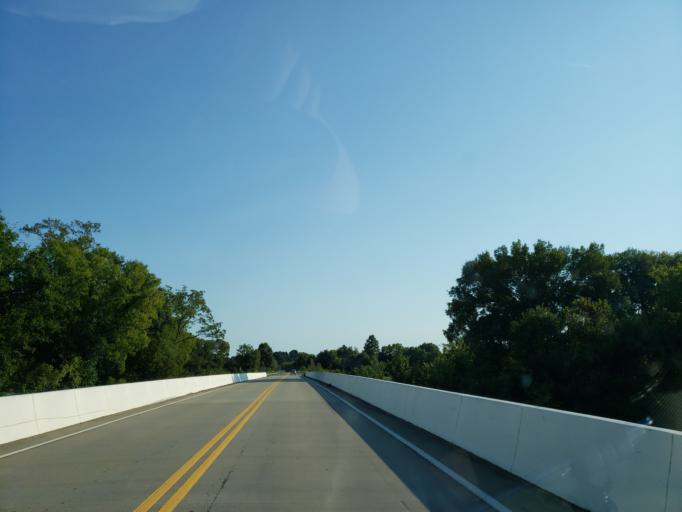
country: US
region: Tennessee
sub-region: Bradley County
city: Wildwood Lake
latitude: 34.9912
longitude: -84.7752
